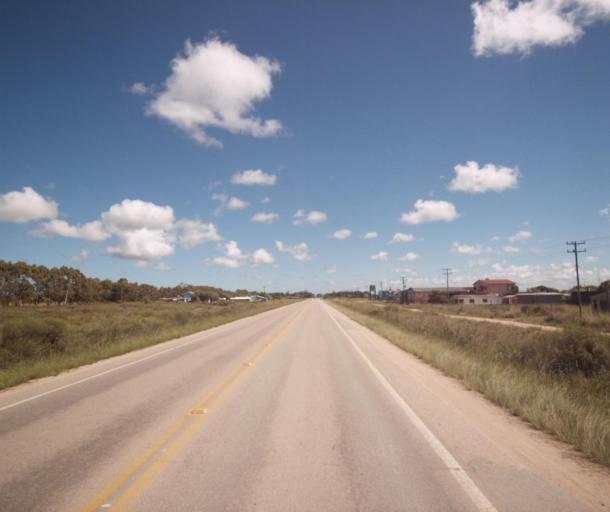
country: BR
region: Rio Grande do Sul
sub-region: Santa Vitoria Do Palmar
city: Santa Vitoria do Palmar
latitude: -33.5276
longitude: -53.3425
